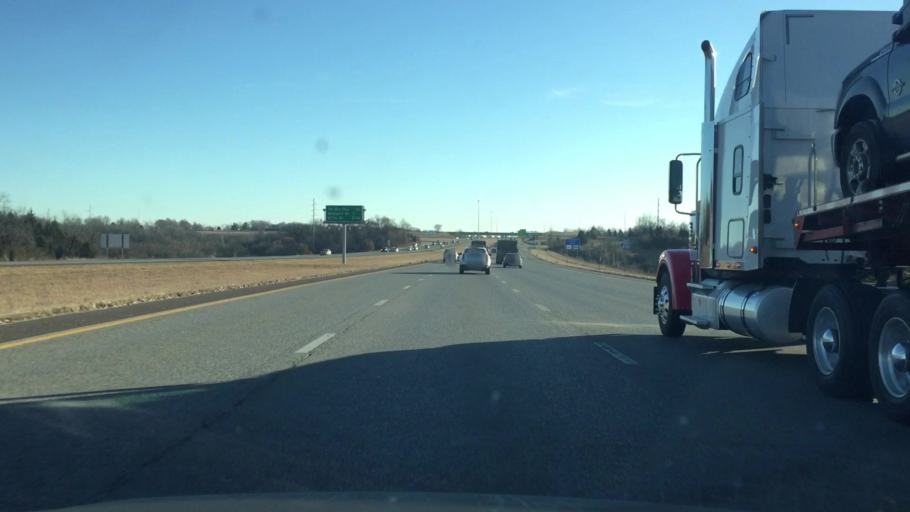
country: US
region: Kansas
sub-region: Wyandotte County
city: Edwardsville
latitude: 39.0213
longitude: -94.7858
